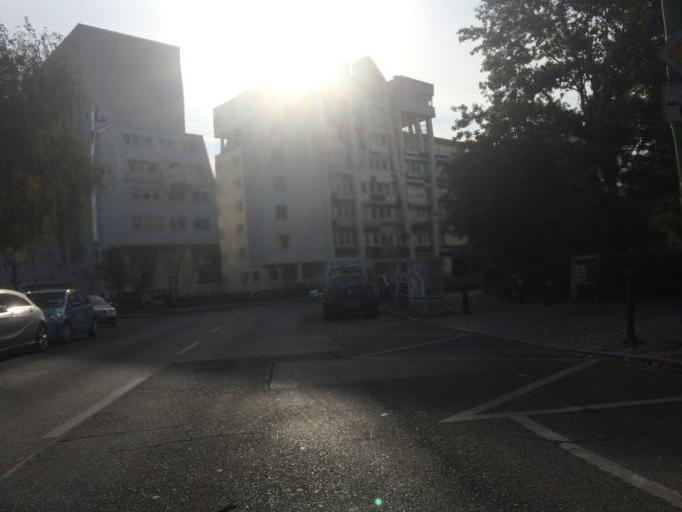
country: DE
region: Berlin
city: Alt-Hohenschoenhausen
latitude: 52.5364
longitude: 13.4908
